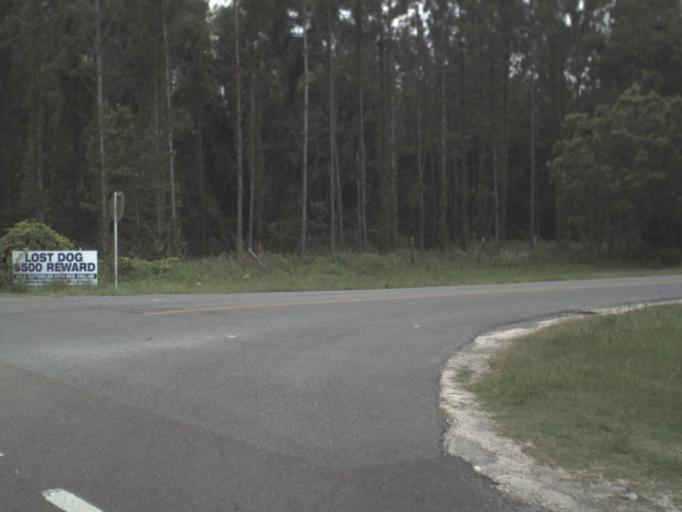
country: US
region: Florida
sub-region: Levy County
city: Manatee Road
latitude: 29.4967
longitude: -82.8896
